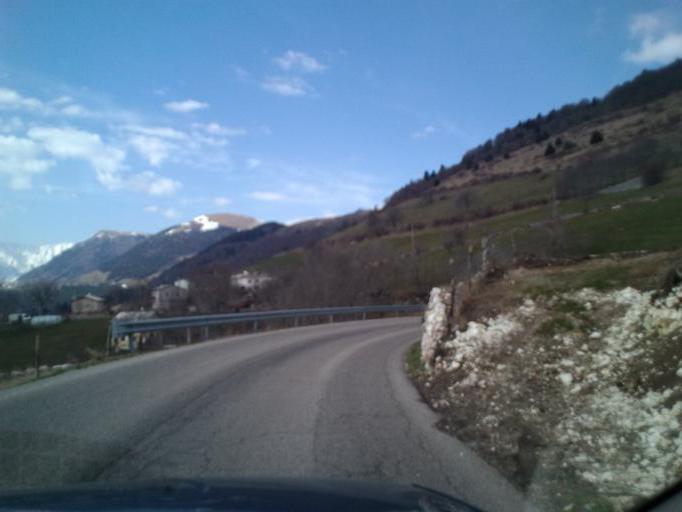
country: IT
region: Veneto
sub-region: Provincia di Verona
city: Erbezzo
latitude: 45.6502
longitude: 10.9885
